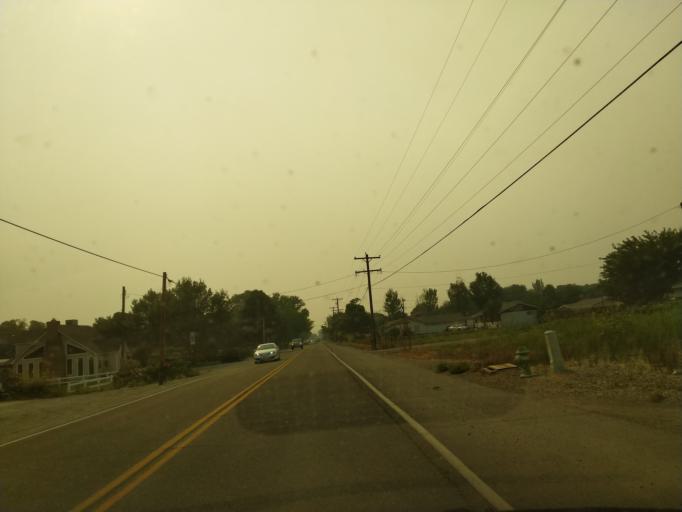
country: US
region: Colorado
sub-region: Mesa County
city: Fruitvale
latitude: 39.0846
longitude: -108.4869
